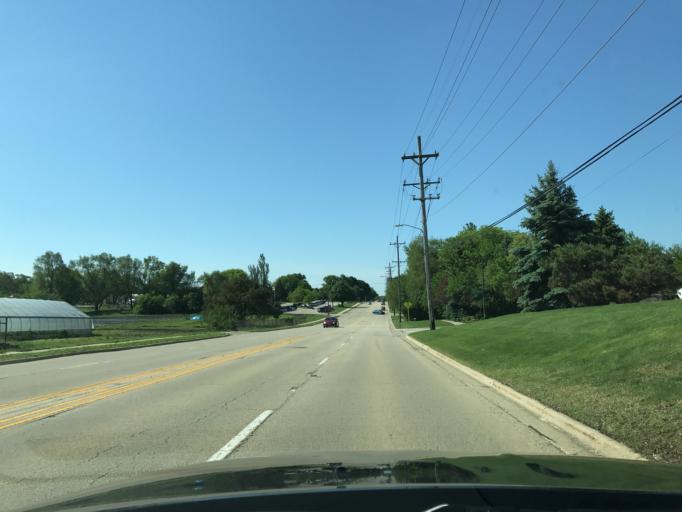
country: US
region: Illinois
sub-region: DuPage County
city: Naperville
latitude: 41.7932
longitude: -88.1545
